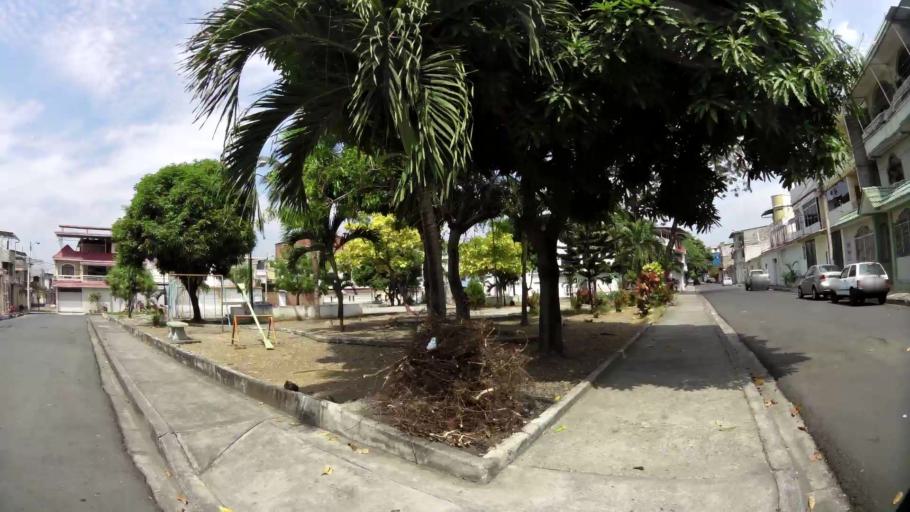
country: EC
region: Guayas
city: Eloy Alfaro
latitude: -2.1214
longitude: -79.9024
